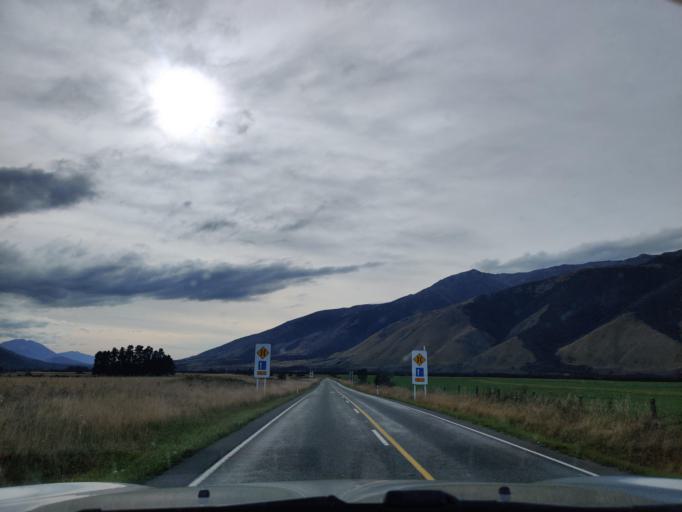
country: NZ
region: Tasman
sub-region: Tasman District
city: Wakefield
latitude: -41.7677
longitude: 172.9625
